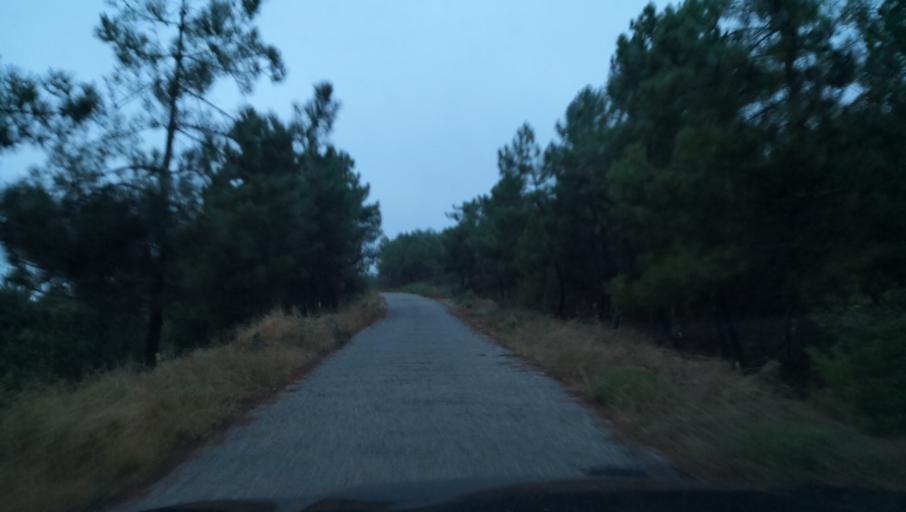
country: PT
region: Vila Real
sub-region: Sabrosa
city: Sabrosa
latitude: 41.2821
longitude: -7.5830
